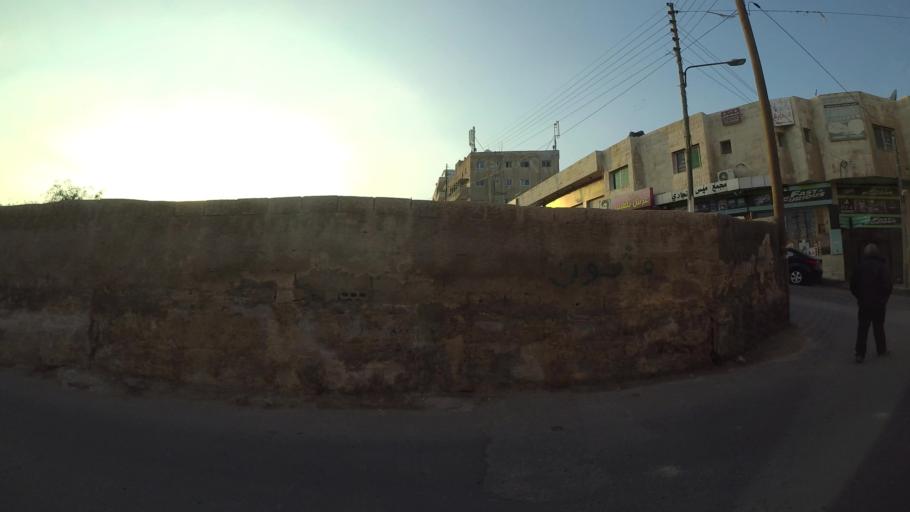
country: JO
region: Amman
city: Amman
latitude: 31.9984
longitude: 35.9473
